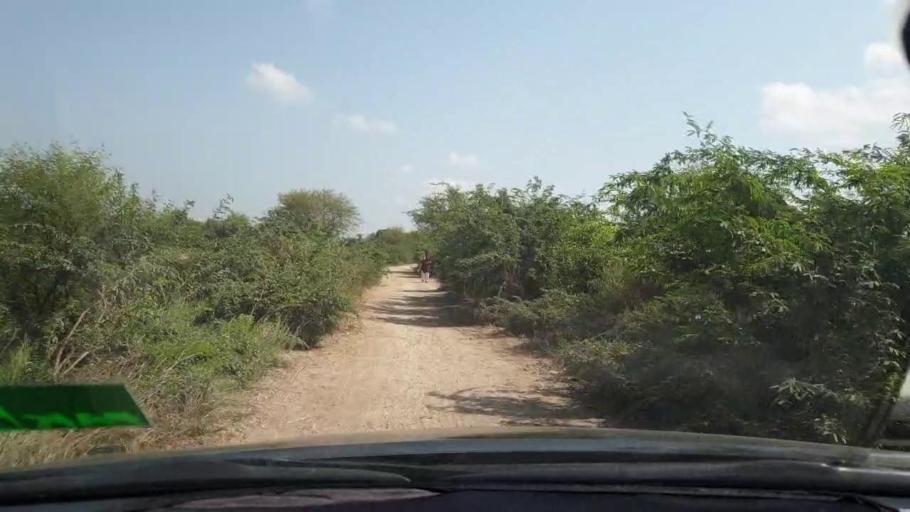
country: PK
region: Sindh
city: Tando Bago
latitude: 24.9304
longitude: 69.0590
